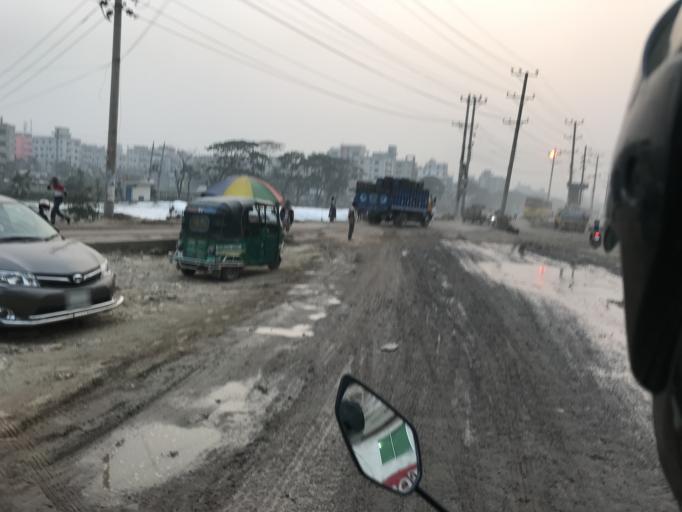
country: BD
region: Dhaka
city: Paltan
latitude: 23.7178
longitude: 90.4743
